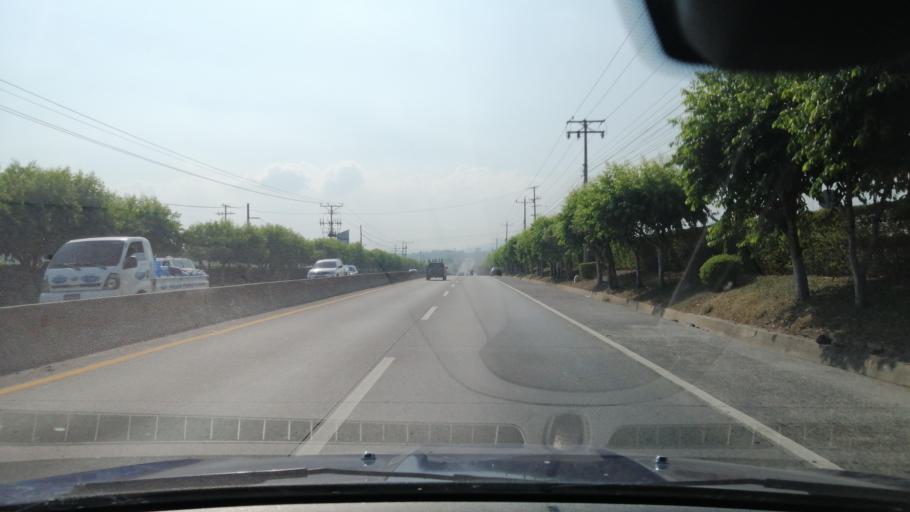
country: SV
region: San Salvador
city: Apopa
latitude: 13.7962
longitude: -89.2279
